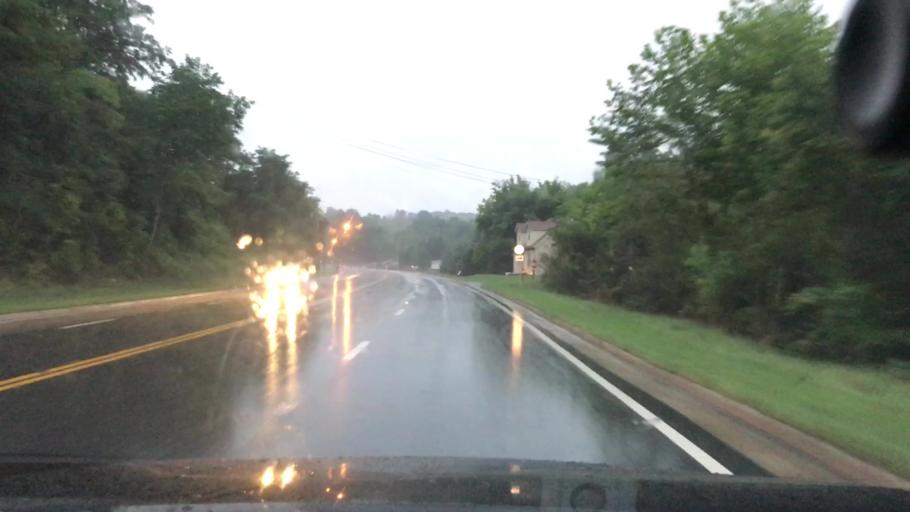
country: US
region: Virginia
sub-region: Giles County
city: Pembroke
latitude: 37.3202
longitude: -80.6238
